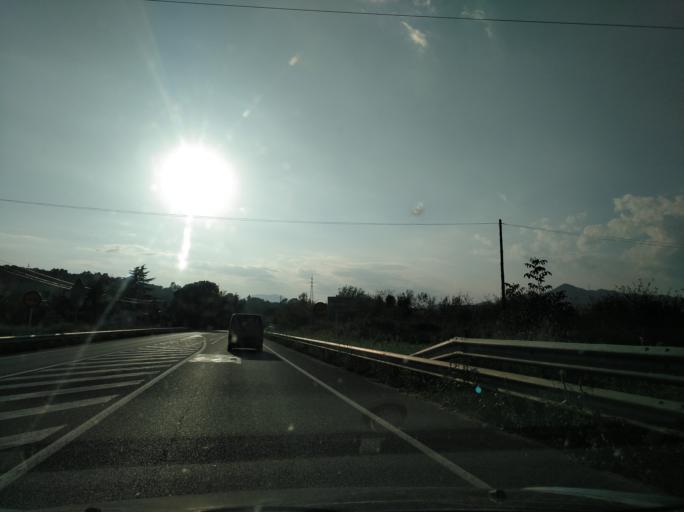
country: ES
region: Catalonia
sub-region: Provincia de Girona
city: Vilablareix
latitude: 41.9697
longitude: 2.7683
